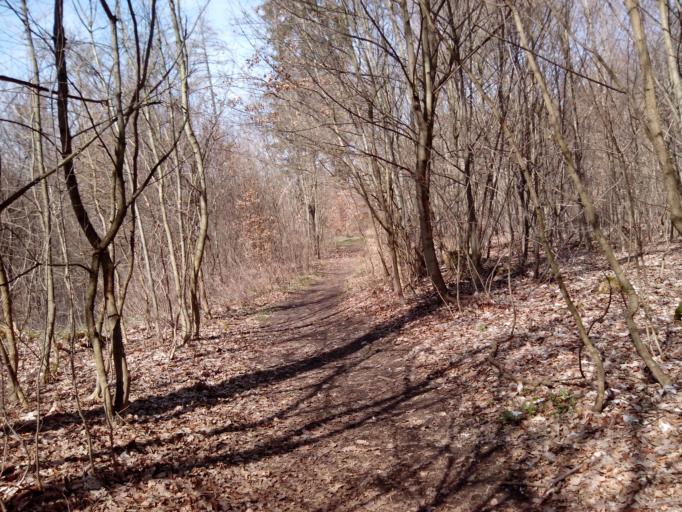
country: CZ
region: Central Bohemia
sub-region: Okres Beroun
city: Beroun
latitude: 49.9349
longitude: 14.1094
